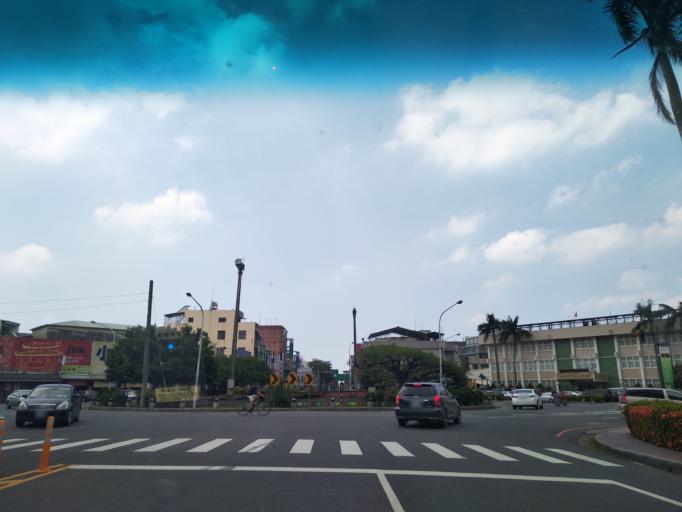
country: TW
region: Taiwan
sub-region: Tainan
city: Tainan
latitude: 22.9667
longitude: 120.2949
